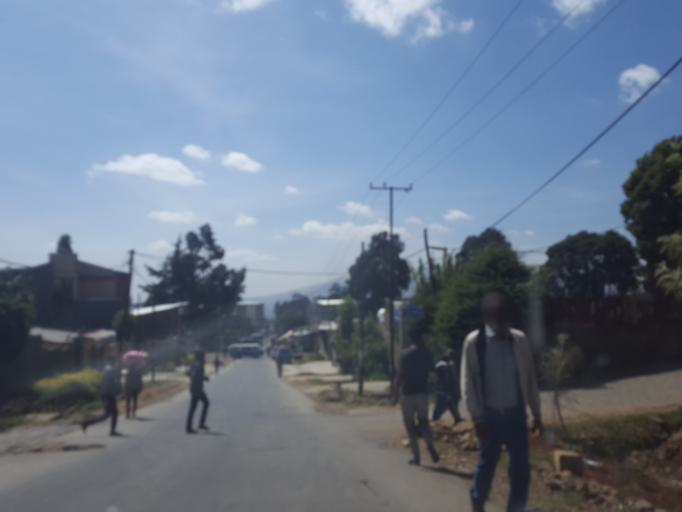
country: ET
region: Adis Abeba
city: Addis Ababa
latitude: 9.0609
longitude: 38.7313
